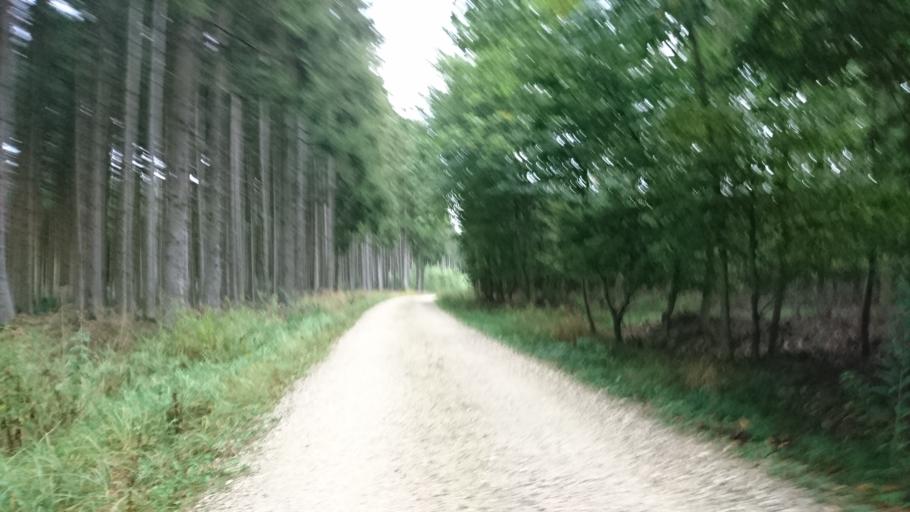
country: DE
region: Bavaria
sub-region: Swabia
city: Welden
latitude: 48.4380
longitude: 10.6249
